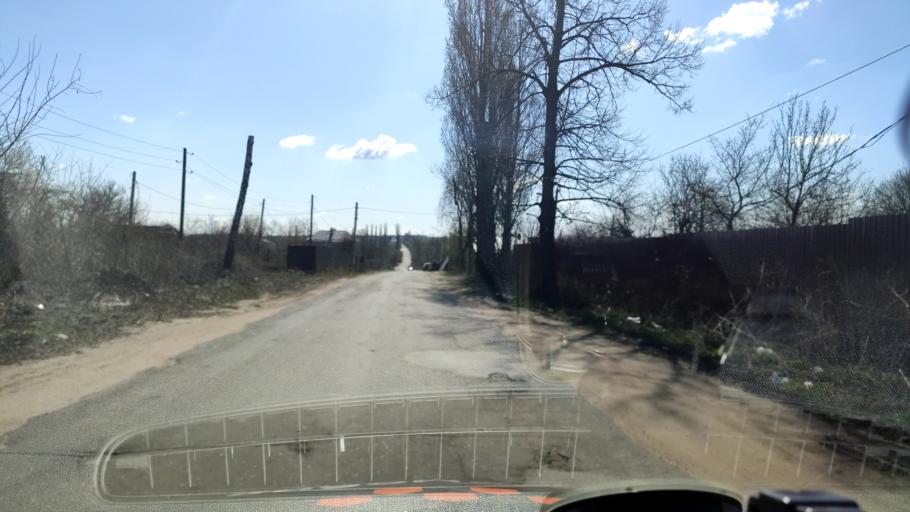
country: RU
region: Voronezj
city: Shilovo
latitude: 51.5978
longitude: 39.1479
